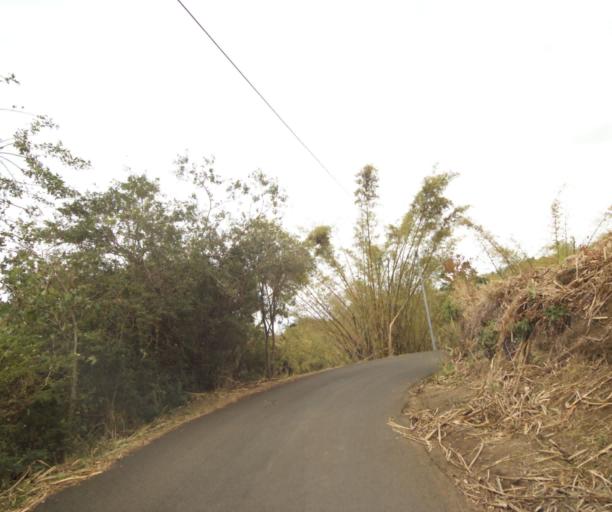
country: RE
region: Reunion
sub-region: Reunion
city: Saint-Paul
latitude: -21.0295
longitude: 55.3010
